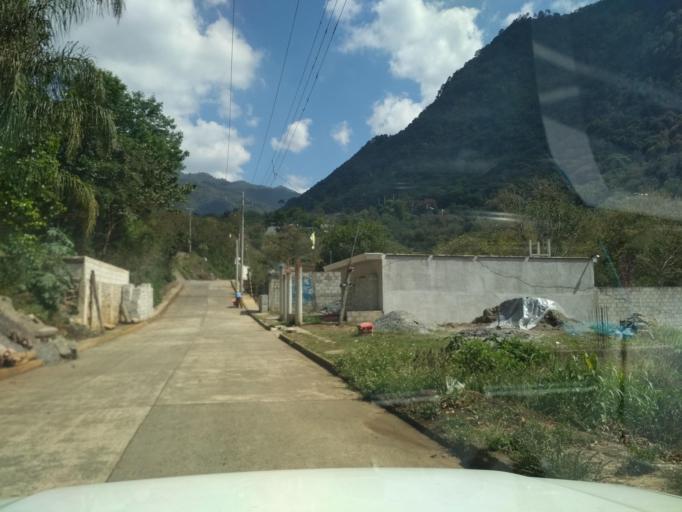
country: MX
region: Veracruz
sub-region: Tlilapan
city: Tonalixco
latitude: 18.7888
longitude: -97.0911
